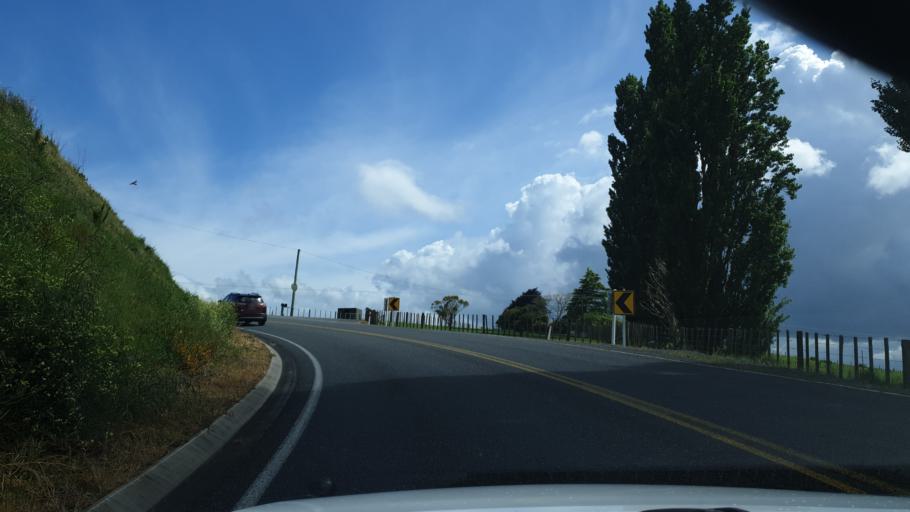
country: NZ
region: Waikato
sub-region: Matamata-Piako District
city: Matamata
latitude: -37.8722
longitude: 175.6862
